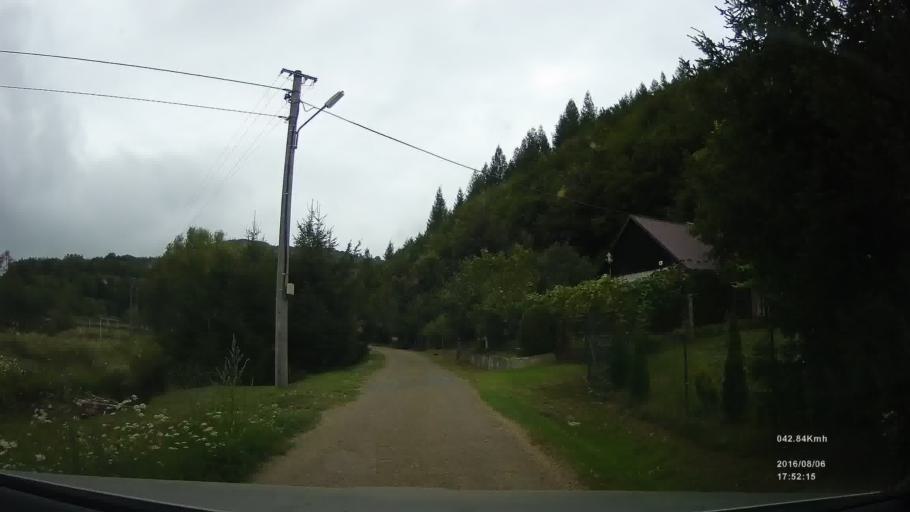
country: SK
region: Presovsky
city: Svidnik
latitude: 49.4044
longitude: 21.5675
